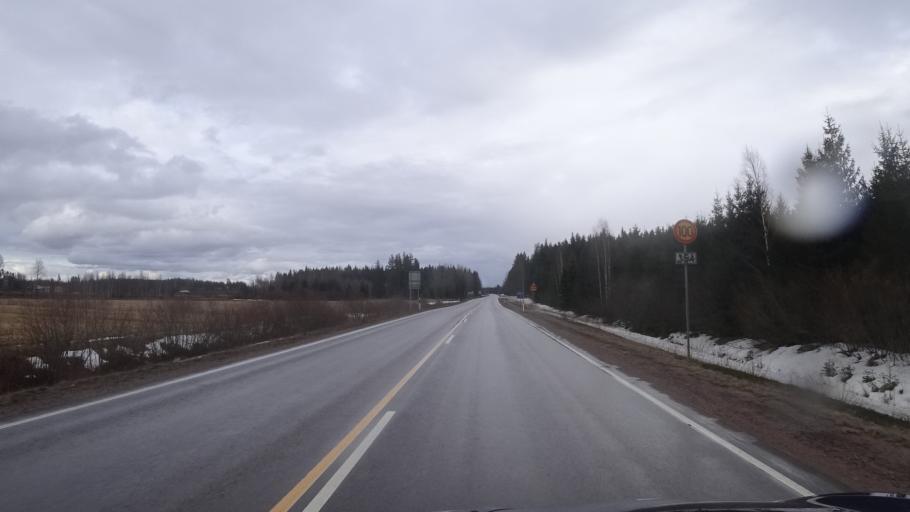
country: FI
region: Kymenlaakso
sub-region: Kouvola
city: Elimaeki
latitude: 60.6906
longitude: 26.5712
